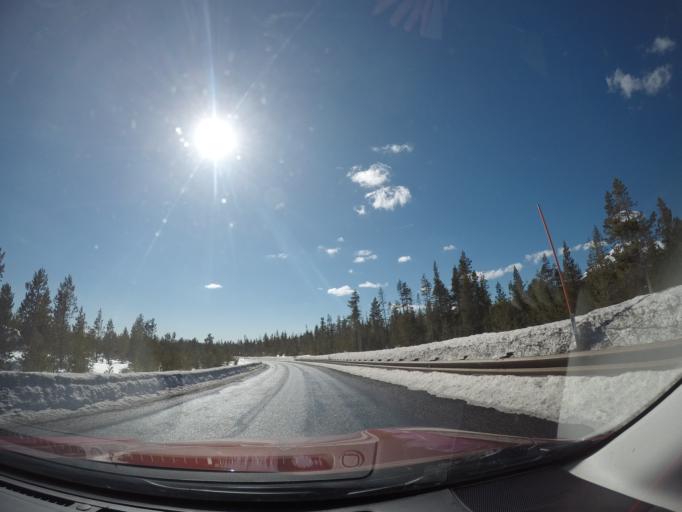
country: US
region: Oregon
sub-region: Deschutes County
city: Sunriver
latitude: 43.9709
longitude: -121.6162
